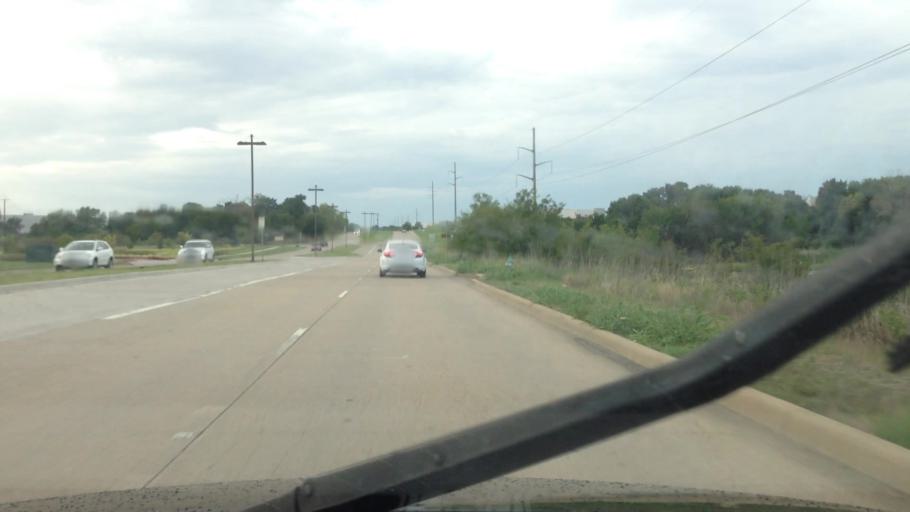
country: US
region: Texas
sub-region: Dallas County
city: Coppell
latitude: 32.9864
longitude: -97.0288
